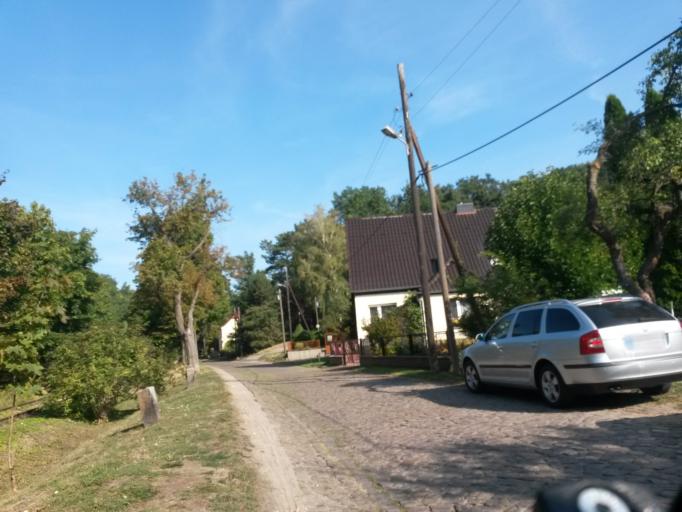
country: DE
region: Saxony-Anhalt
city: Nudersdorf
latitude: 51.9149
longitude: 12.5945
